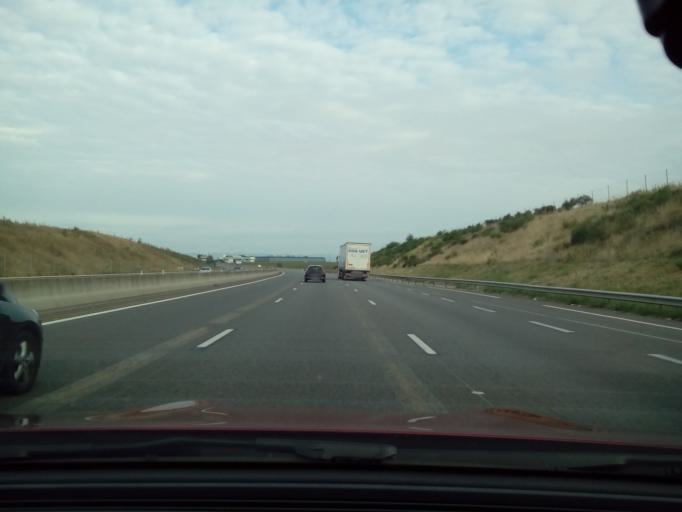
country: FR
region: Rhone-Alpes
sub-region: Departement de l'Ain
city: Civrieux
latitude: 45.8965
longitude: 4.8875
